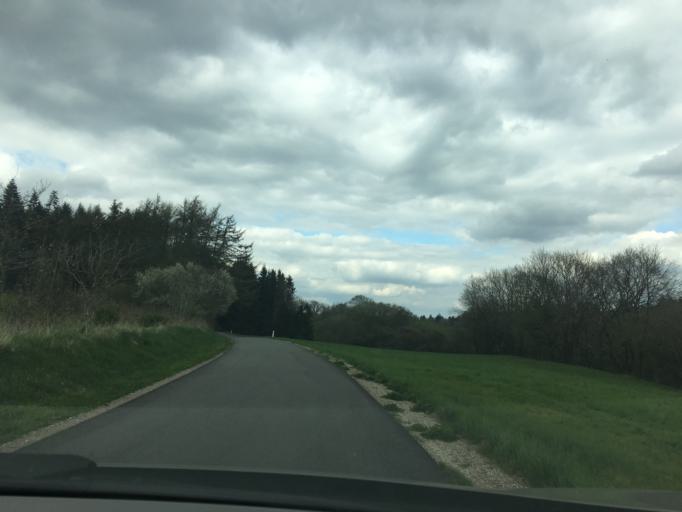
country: DK
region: Central Jutland
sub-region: Horsens Kommune
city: Braedstrup
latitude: 55.9580
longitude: 9.6870
